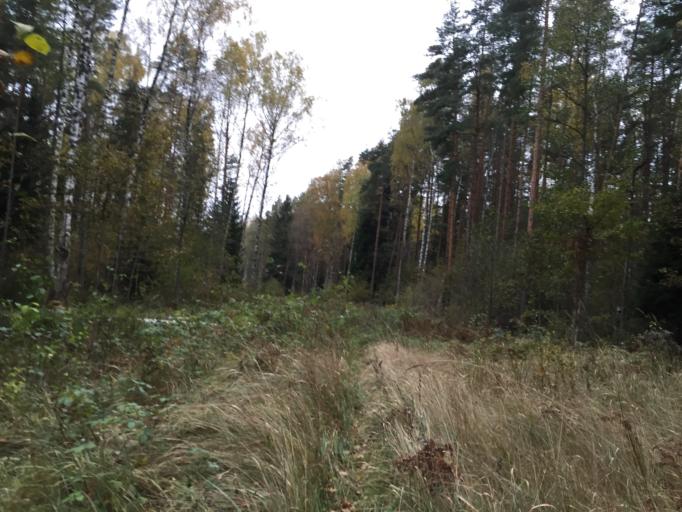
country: LV
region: Jelgava
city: Jelgava
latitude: 56.6353
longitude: 23.6409
